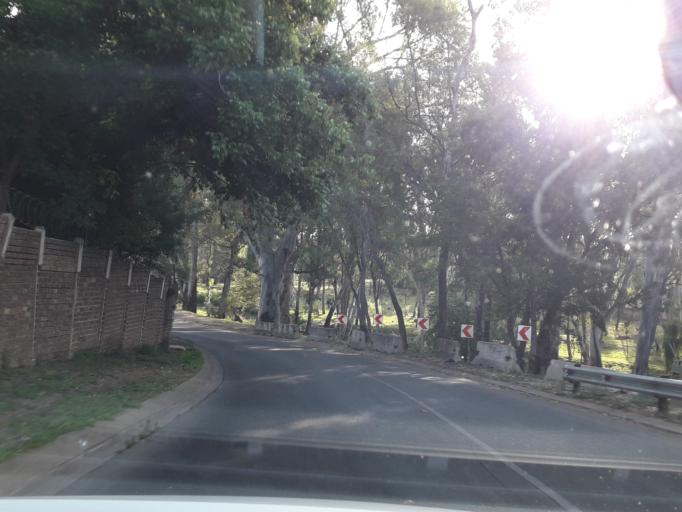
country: ZA
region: Gauteng
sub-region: City of Johannesburg Metropolitan Municipality
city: Diepsloot
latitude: -26.0526
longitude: 27.9885
